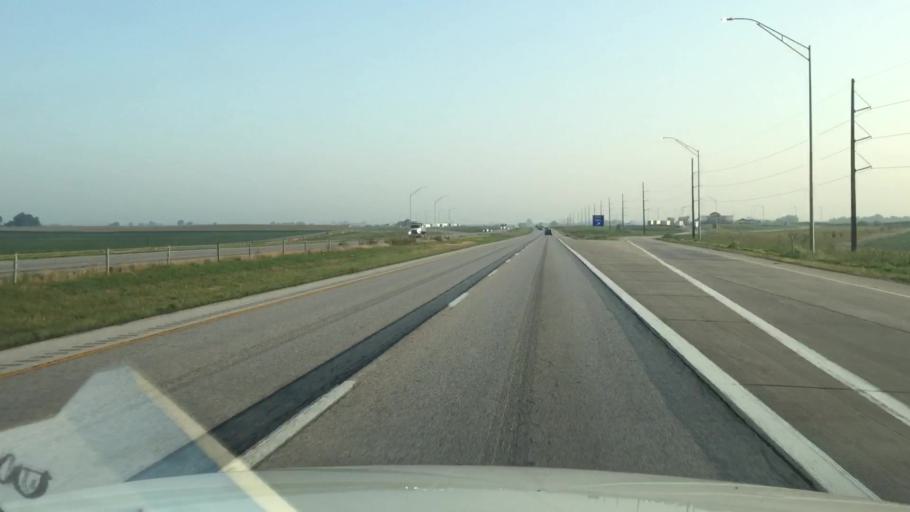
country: US
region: Iowa
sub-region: Story County
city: Huxley
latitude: 41.8231
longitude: -93.5708
